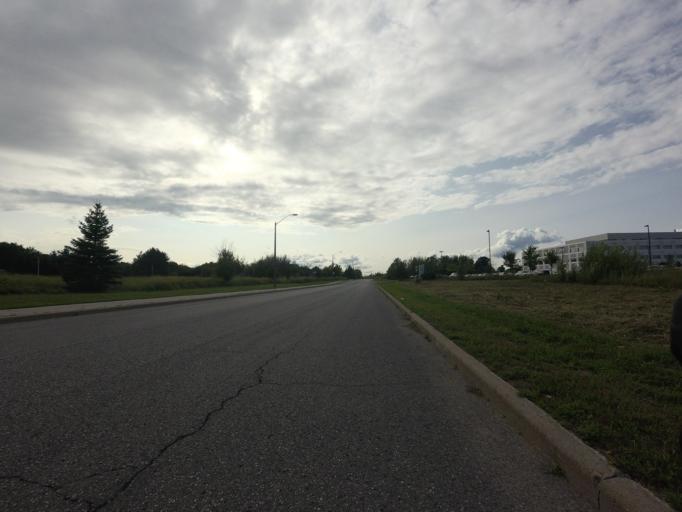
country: CA
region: Ontario
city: Ottawa
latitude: 45.2948
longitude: -75.7098
